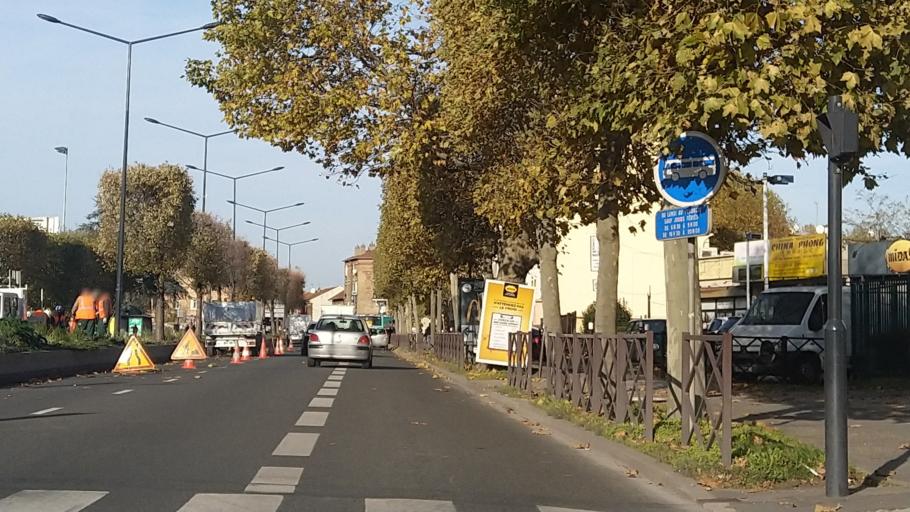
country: FR
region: Ile-de-France
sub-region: Departement de Seine-Saint-Denis
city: Stains
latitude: 48.9477
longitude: 2.3864
